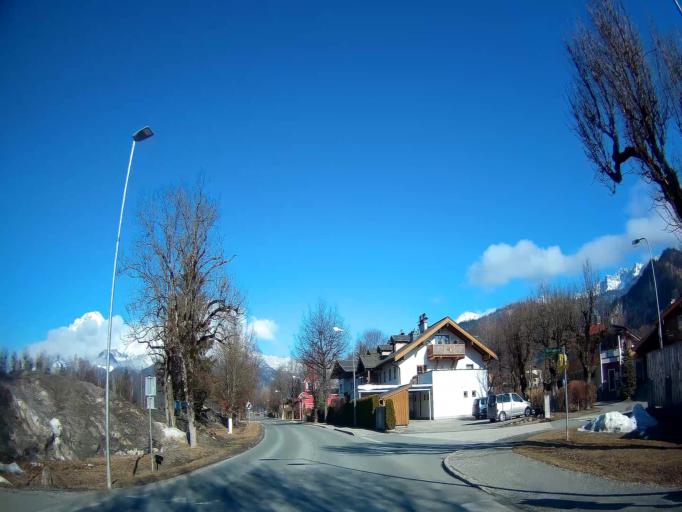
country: AT
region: Salzburg
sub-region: Politischer Bezirk Zell am See
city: Saalfelden am Steinernen Meer
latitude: 47.4314
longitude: 12.8520
